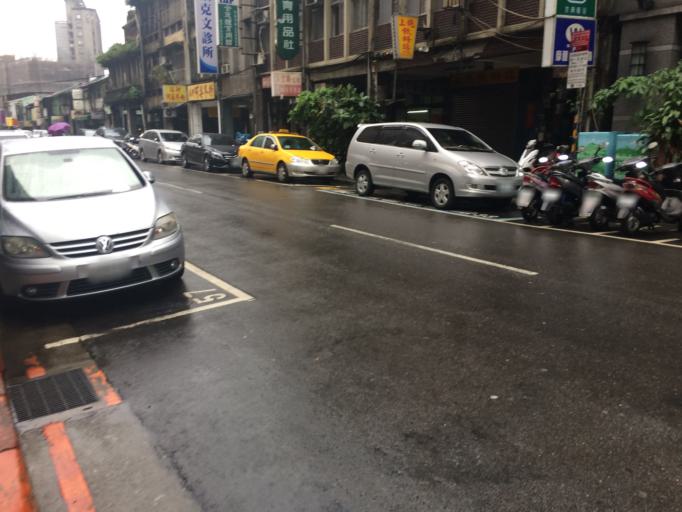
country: TW
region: Taipei
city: Taipei
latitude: 25.0399
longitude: 121.5037
